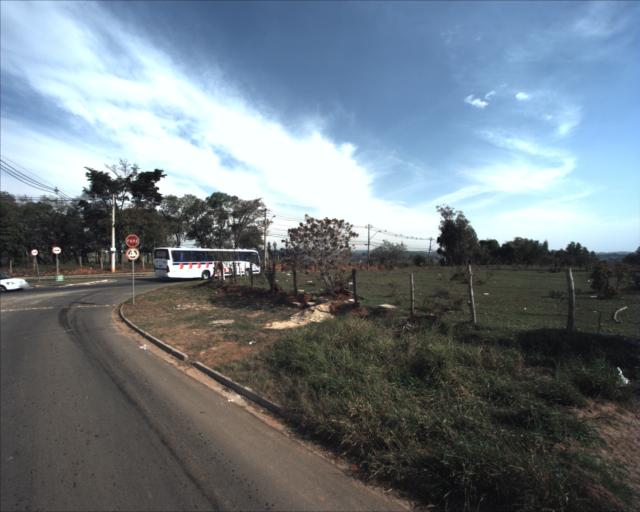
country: BR
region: Sao Paulo
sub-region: Sorocaba
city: Sorocaba
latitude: -23.4956
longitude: -47.5326
